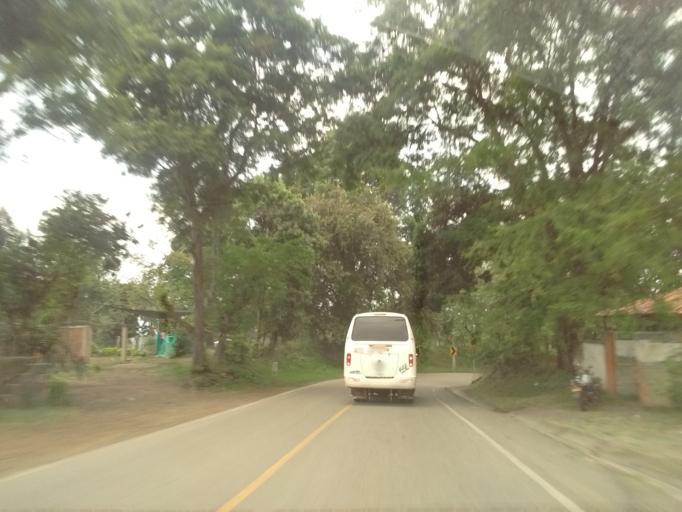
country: CO
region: Cauca
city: Caloto
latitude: 3.0645
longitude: -76.3663
